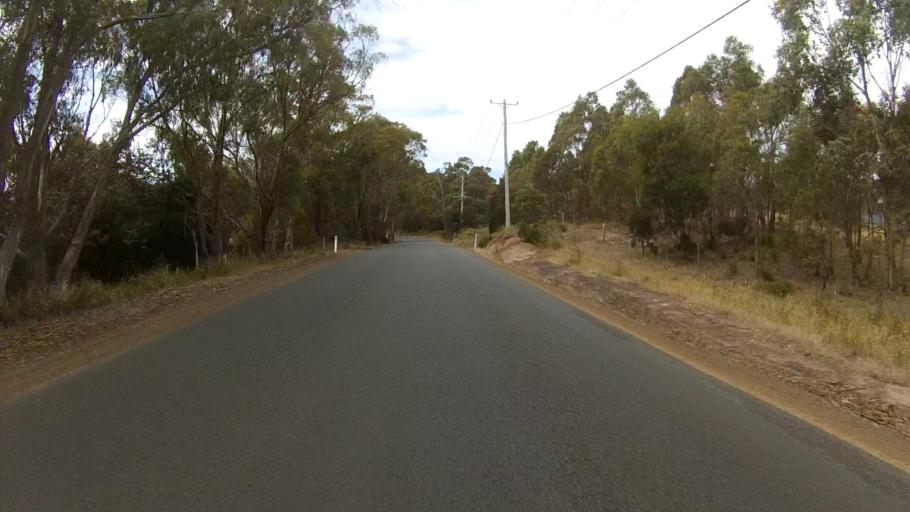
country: AU
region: Tasmania
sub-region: Kingborough
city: Blackmans Bay
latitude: -43.0234
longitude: 147.3065
